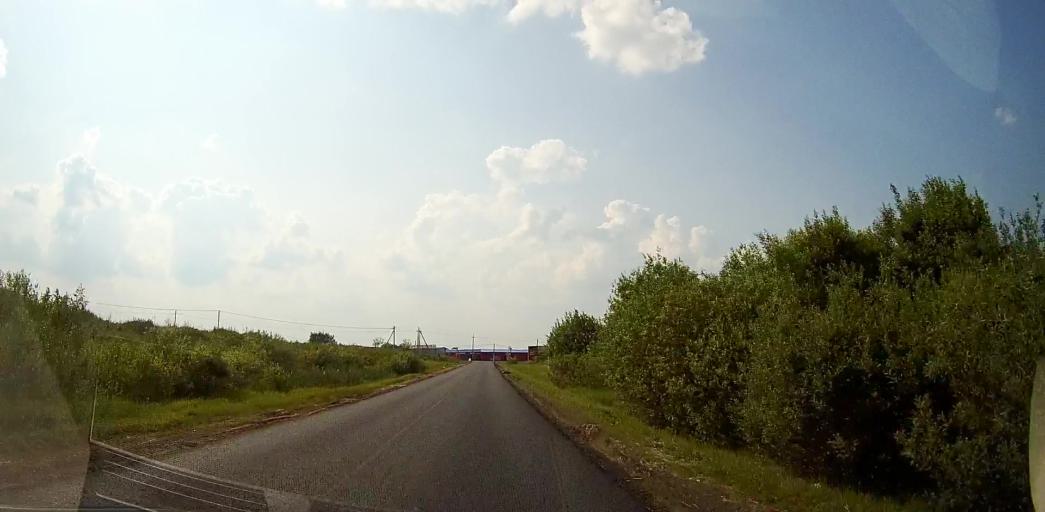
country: RU
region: Moskovskaya
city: Il'inskoye
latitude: 55.2218
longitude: 37.9299
